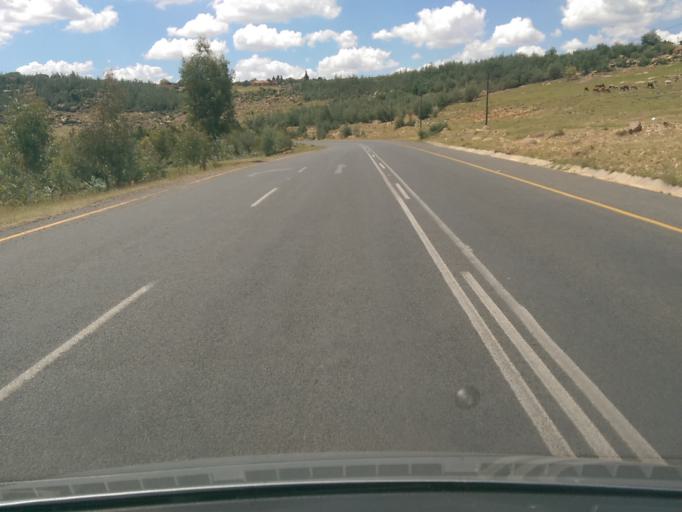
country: LS
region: Maseru
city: Maseru
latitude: -29.3973
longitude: 27.5291
